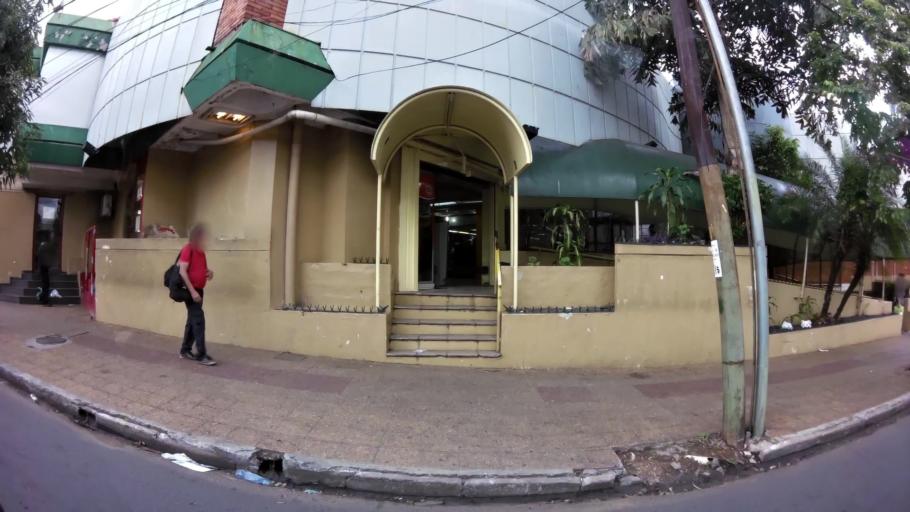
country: PY
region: Asuncion
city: Asuncion
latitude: -25.2897
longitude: -57.5900
